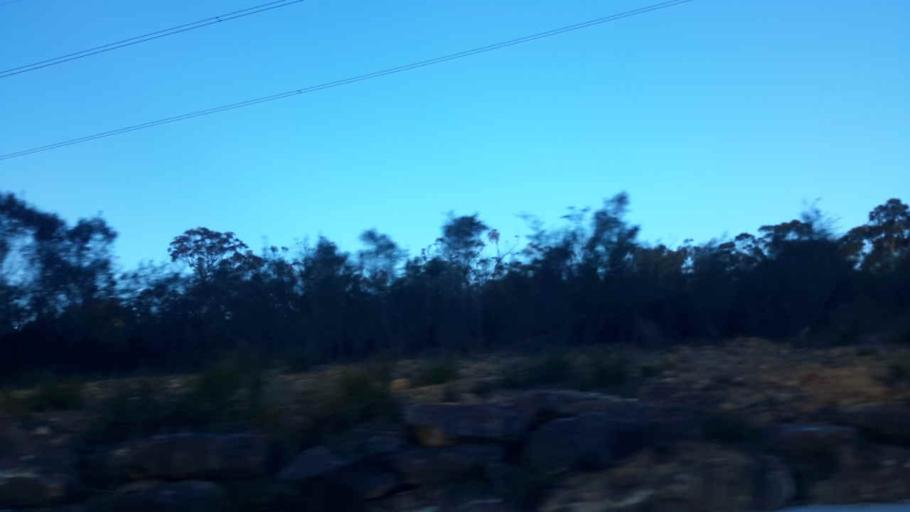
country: AU
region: New South Wales
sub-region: Wollondilly
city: Douglas Park
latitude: -34.2954
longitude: 150.7342
